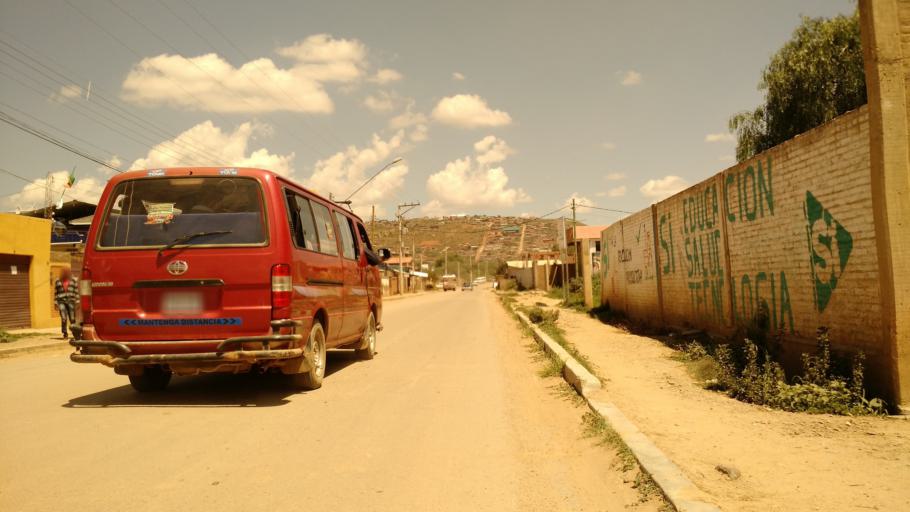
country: BO
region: Cochabamba
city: Cochabamba
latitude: -17.4517
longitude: -66.1558
